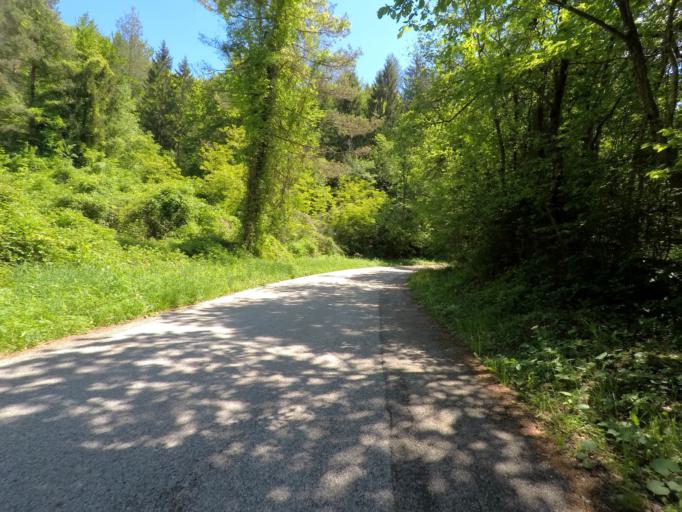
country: IT
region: Friuli Venezia Giulia
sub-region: Provincia di Udine
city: Raveo
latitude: 46.4434
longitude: 12.8811
